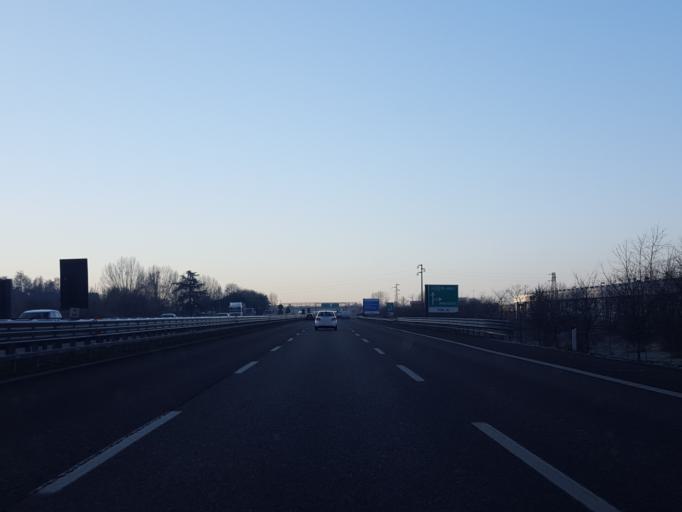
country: IT
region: Veneto
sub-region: Provincia di Vicenza
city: Tavernelle
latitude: 45.4967
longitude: 11.4491
